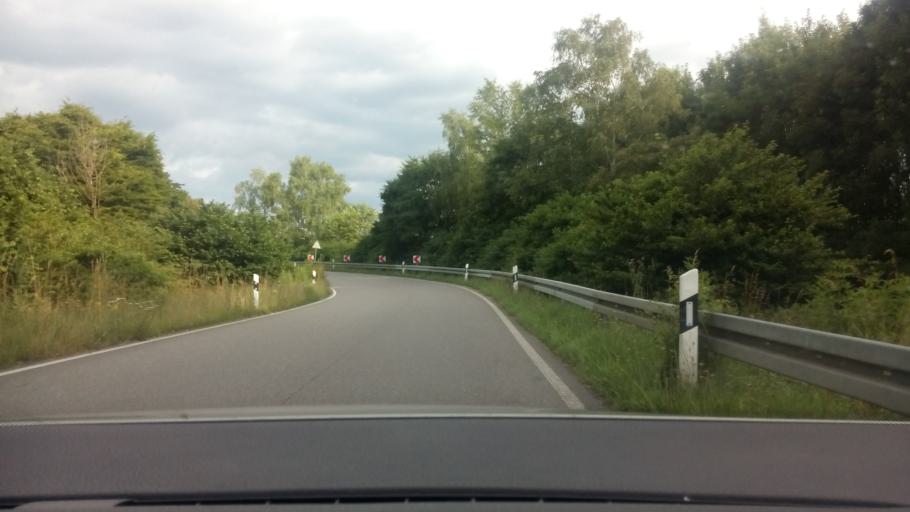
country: DE
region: Bavaria
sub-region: Upper Bavaria
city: Hebertshausen
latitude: 48.2545
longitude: 11.5004
